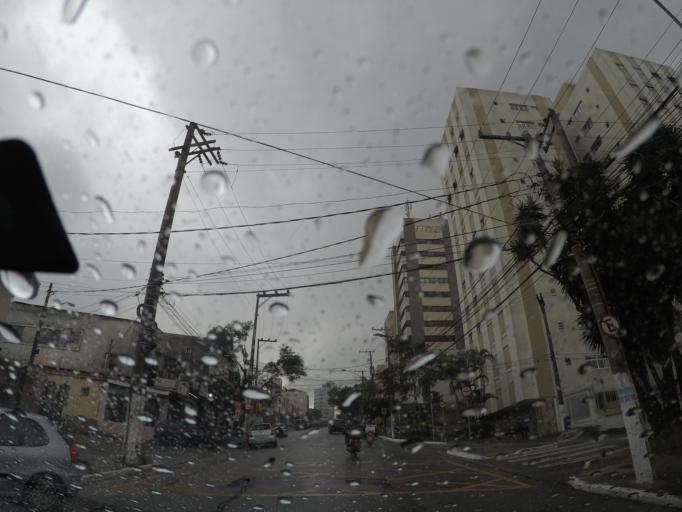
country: BR
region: Sao Paulo
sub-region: Diadema
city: Diadema
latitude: -23.6357
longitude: -46.6444
